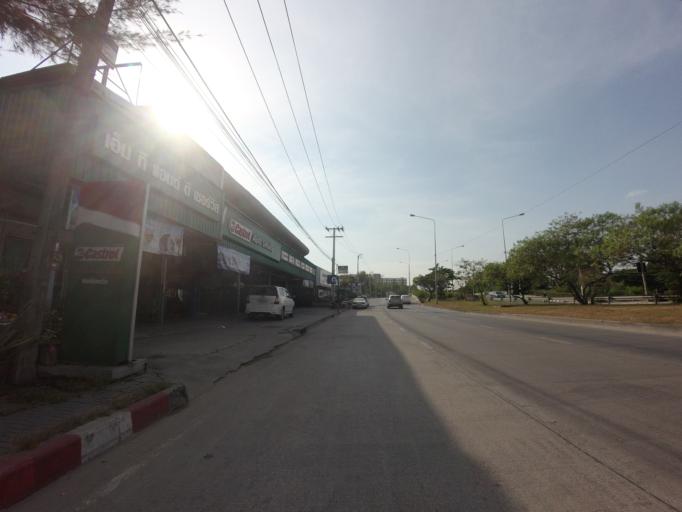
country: TH
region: Bangkok
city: Bang Kapi
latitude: 13.7523
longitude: 100.6336
